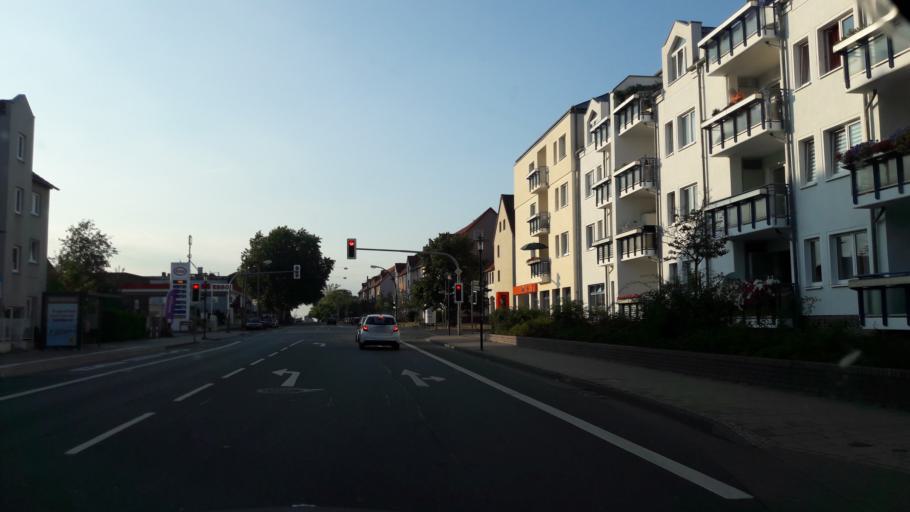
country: DE
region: Lower Saxony
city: Hildesheim
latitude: 52.1652
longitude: 9.9428
